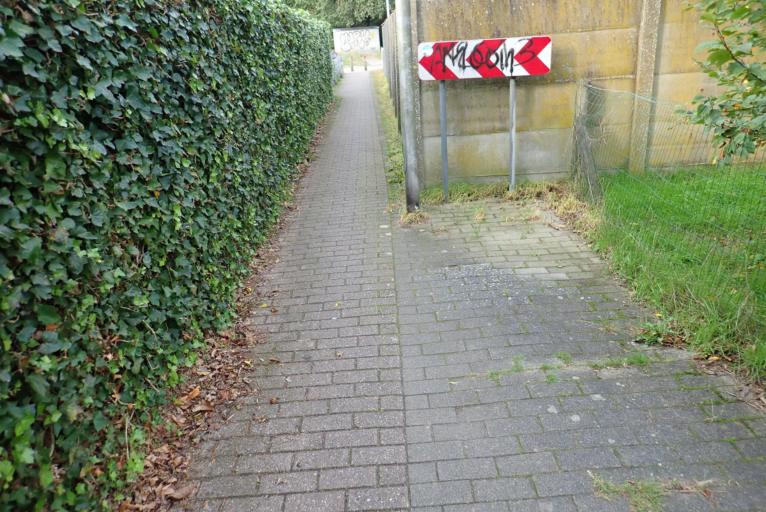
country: BE
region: Flanders
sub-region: Provincie Antwerpen
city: Essen
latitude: 51.4297
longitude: 4.4572
